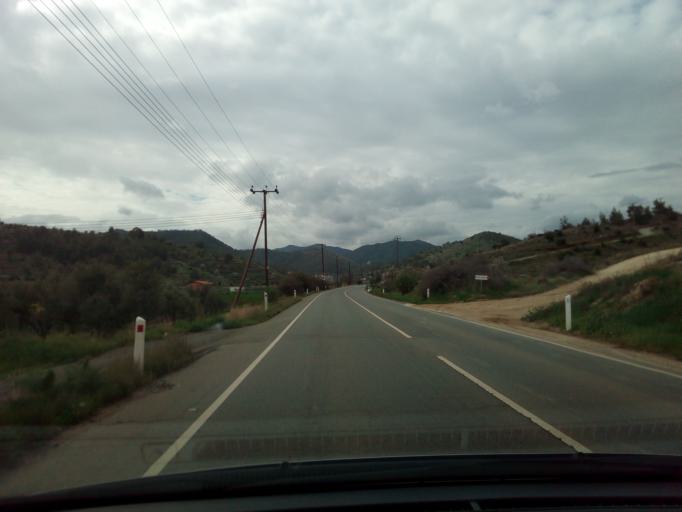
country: CY
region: Lefkosia
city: Klirou
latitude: 35.0127
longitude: 33.1518
